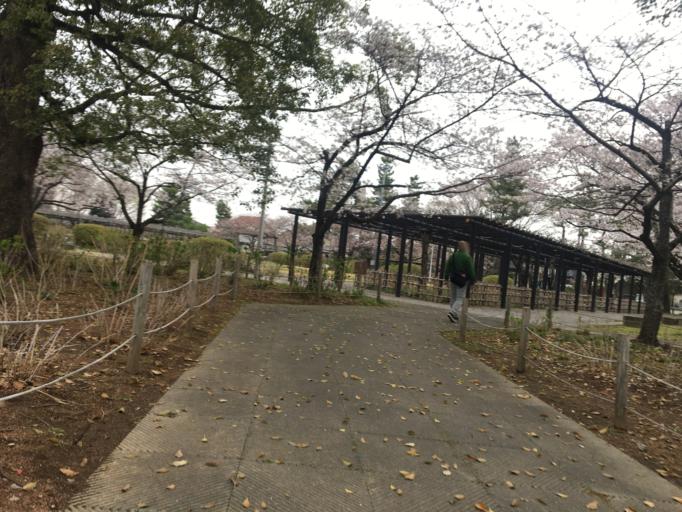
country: JP
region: Saitama
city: Kisai
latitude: 36.1064
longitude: 139.5707
